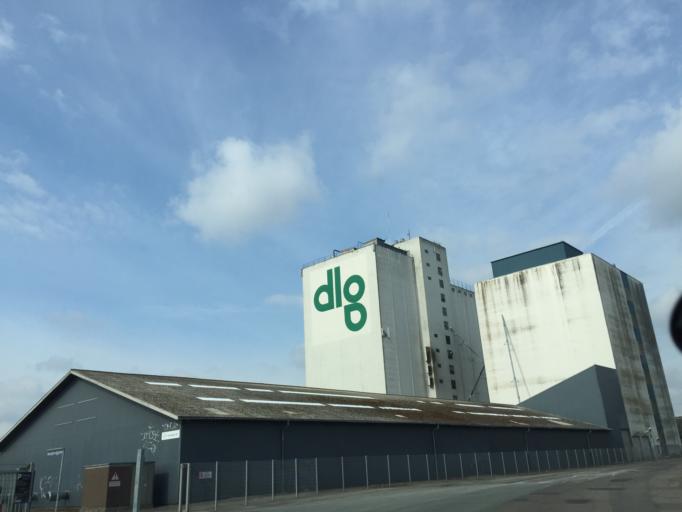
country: DK
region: South Denmark
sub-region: Odense Kommune
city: Odense
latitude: 55.4160
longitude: 10.3805
